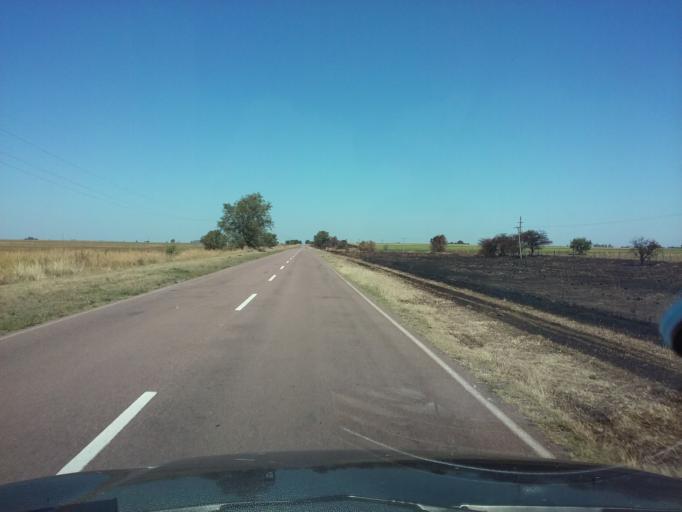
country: AR
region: La Pampa
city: Uriburu
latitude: -36.3861
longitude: -63.9431
